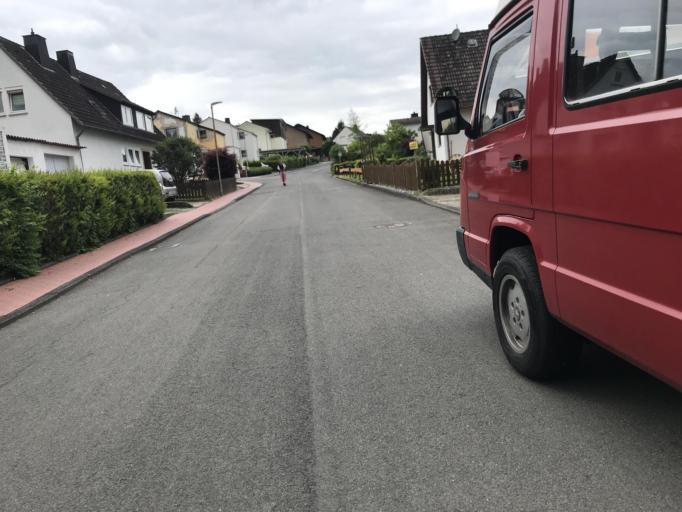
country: DE
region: Hesse
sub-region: Regierungsbezirk Kassel
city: Martinhagen
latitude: 51.2877
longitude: 9.3407
